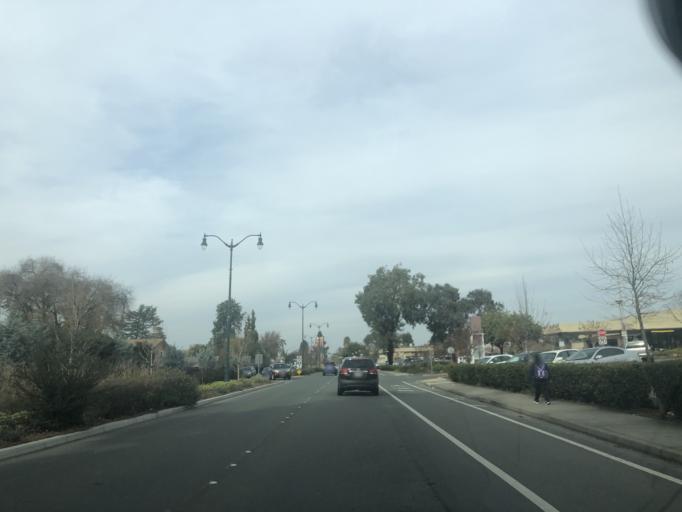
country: US
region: California
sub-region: Contra Costa County
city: Pacheco
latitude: 37.9690
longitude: -122.0629
